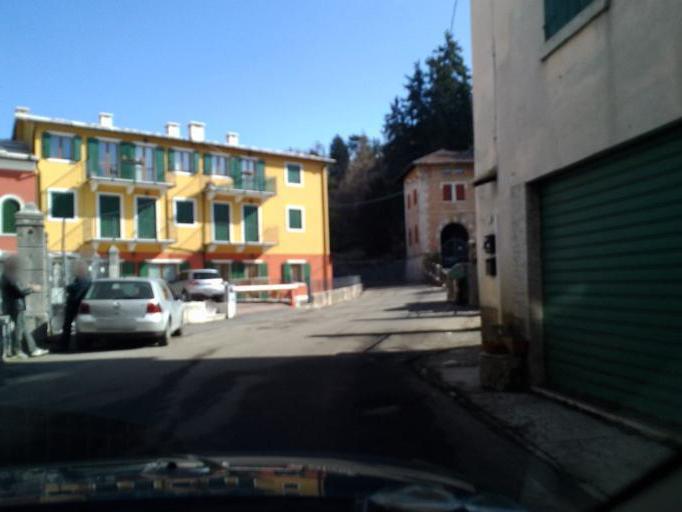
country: IT
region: Veneto
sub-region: Provincia di Verona
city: Bosco Chiesanuova
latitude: 45.6222
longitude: 11.0306
